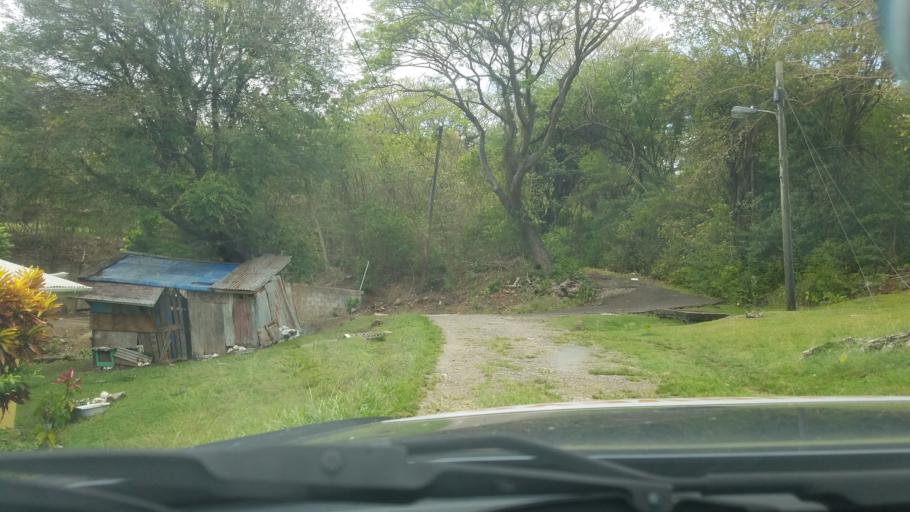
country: LC
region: Gros-Islet
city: Gros Islet
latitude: 14.0610
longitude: -60.9511
